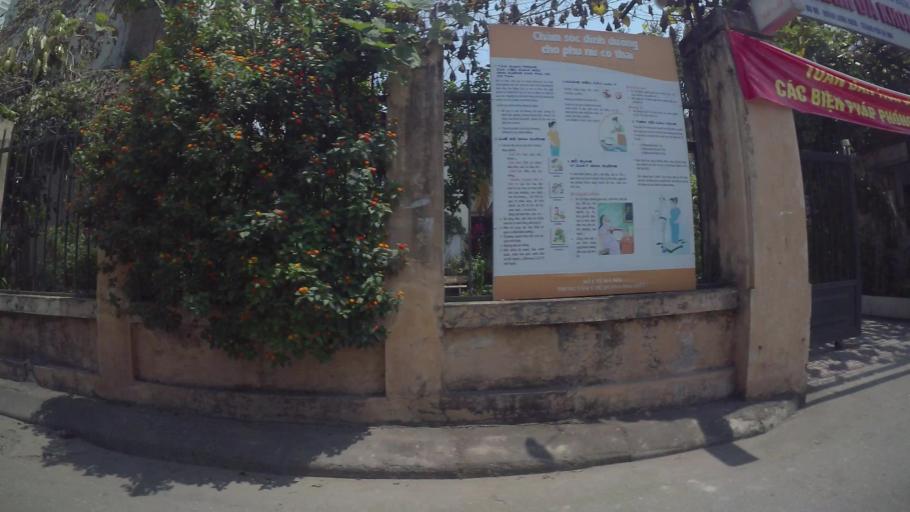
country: VN
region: Ha Noi
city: Hoan Kiem
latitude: 21.0381
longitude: 105.8714
